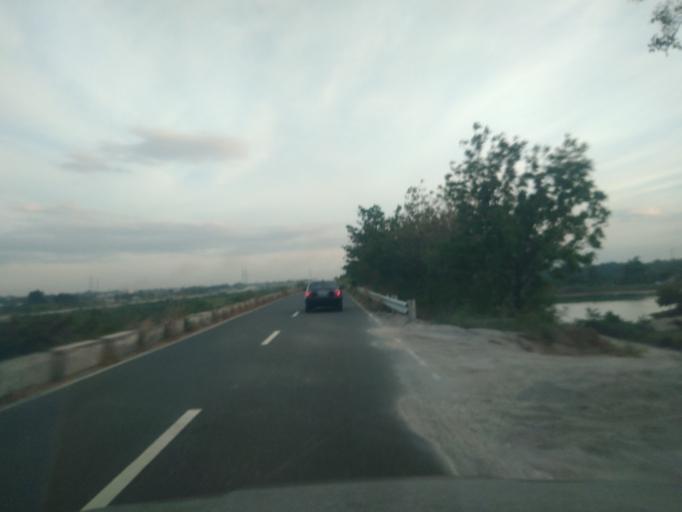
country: PH
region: Central Luzon
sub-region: Province of Pampanga
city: Santa Rita
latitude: 15.0069
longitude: 120.6307
